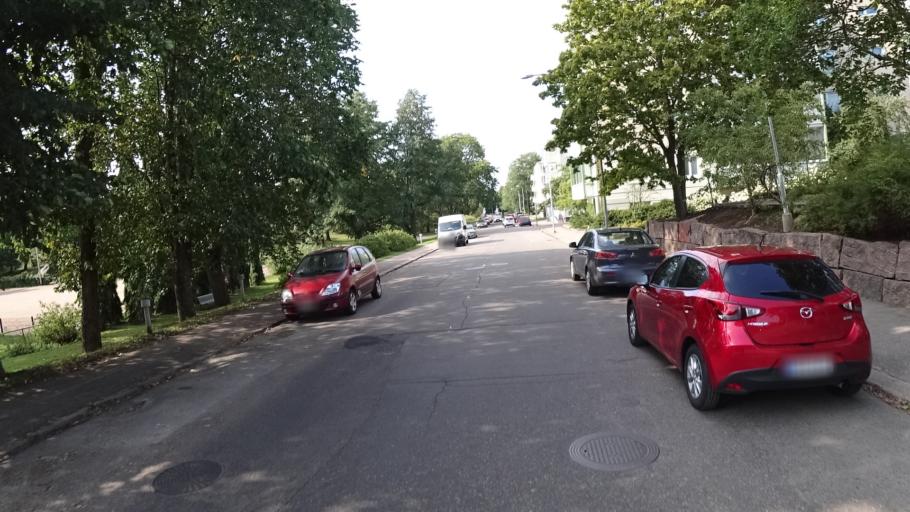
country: FI
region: Kymenlaakso
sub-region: Kotka-Hamina
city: Kotka
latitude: 60.4652
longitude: 26.9517
